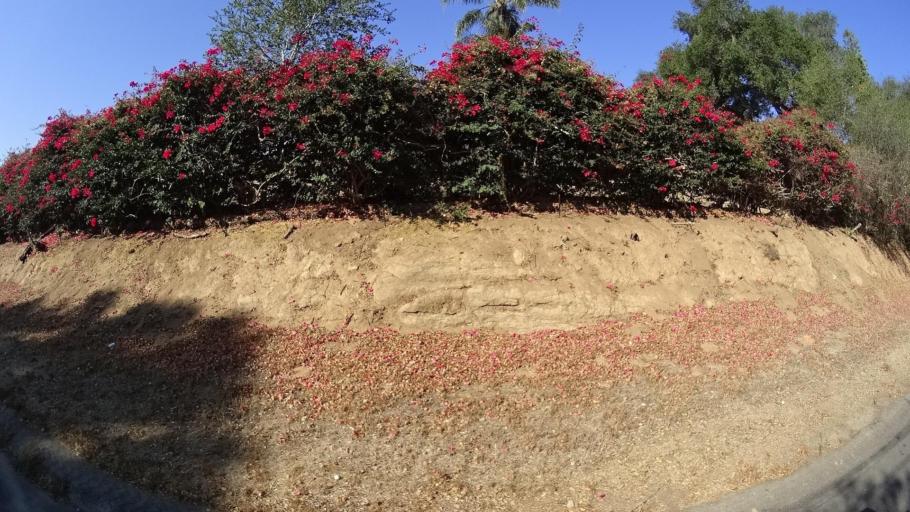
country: US
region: California
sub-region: San Diego County
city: Fallbrook
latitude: 33.3398
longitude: -117.2434
